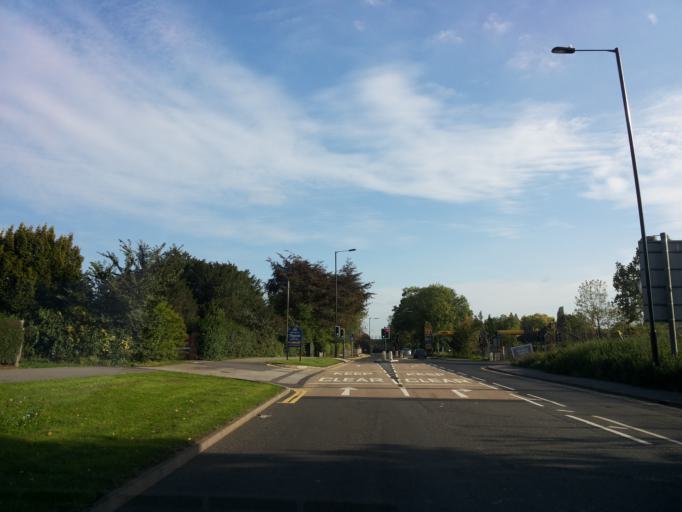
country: GB
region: England
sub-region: Doncaster
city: Hatfield
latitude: 53.6172
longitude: -0.9757
